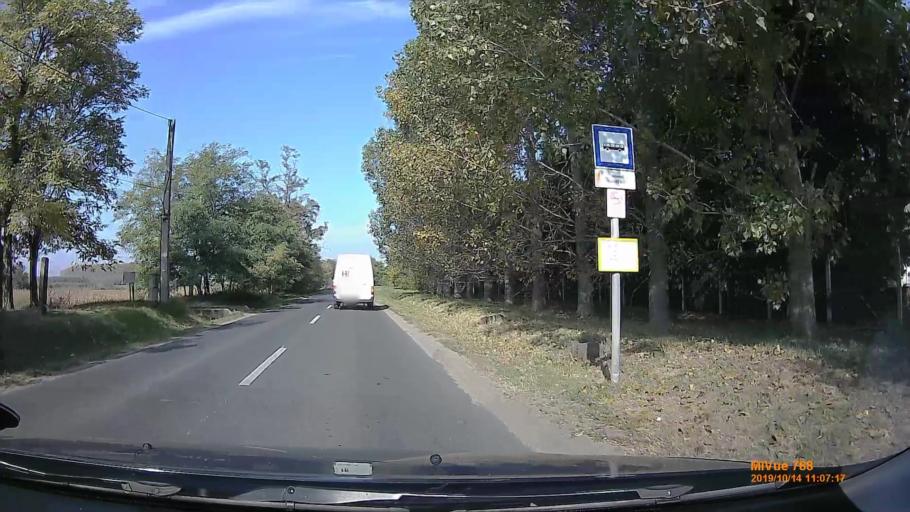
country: HU
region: Pest
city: Monor
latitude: 47.3649
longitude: 19.4281
